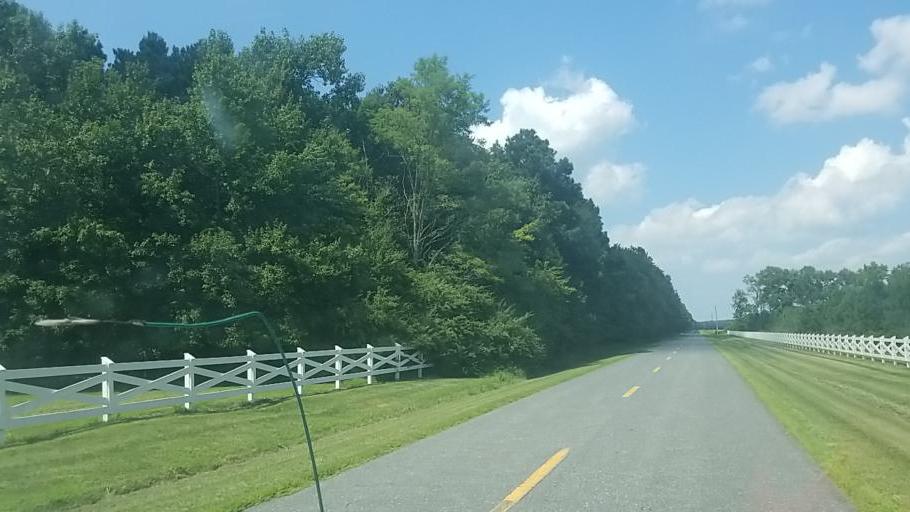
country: US
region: Maryland
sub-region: Wicomico County
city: Hebron
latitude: 38.4542
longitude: -75.8482
